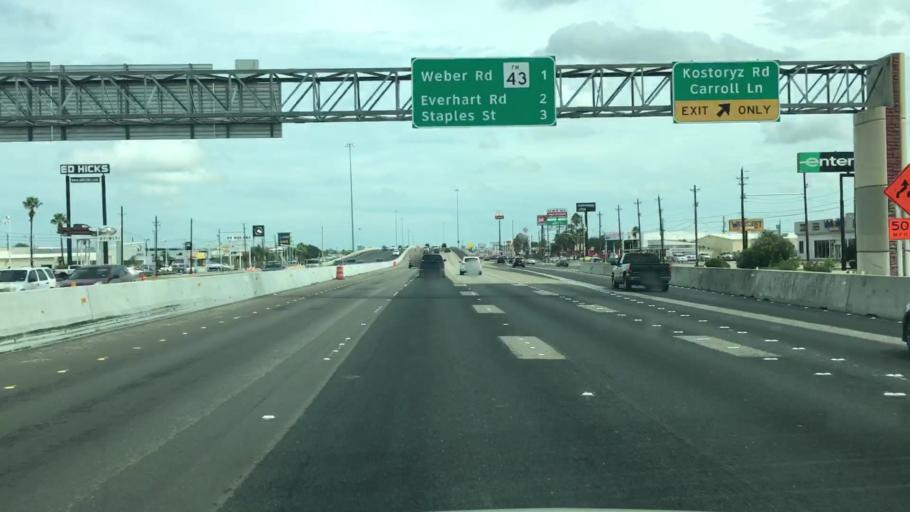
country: US
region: Texas
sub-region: Nueces County
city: Corpus Christi
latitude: 27.7306
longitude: -97.4171
